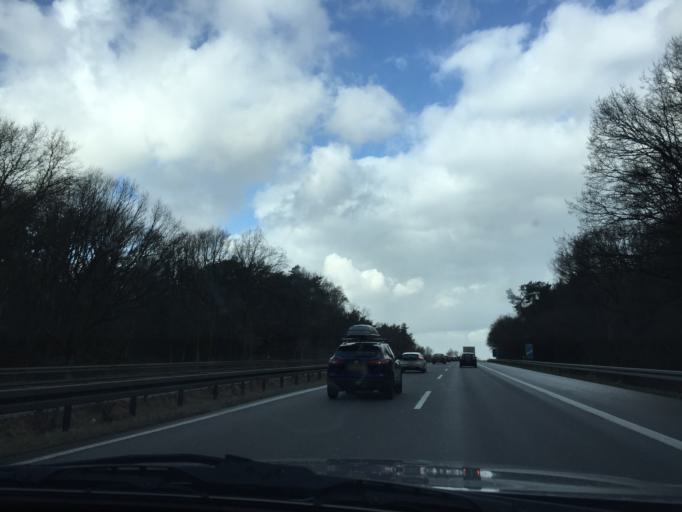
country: NL
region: Gelderland
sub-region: Gemeente Montferland
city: s-Heerenberg
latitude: 51.8798
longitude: 6.1866
